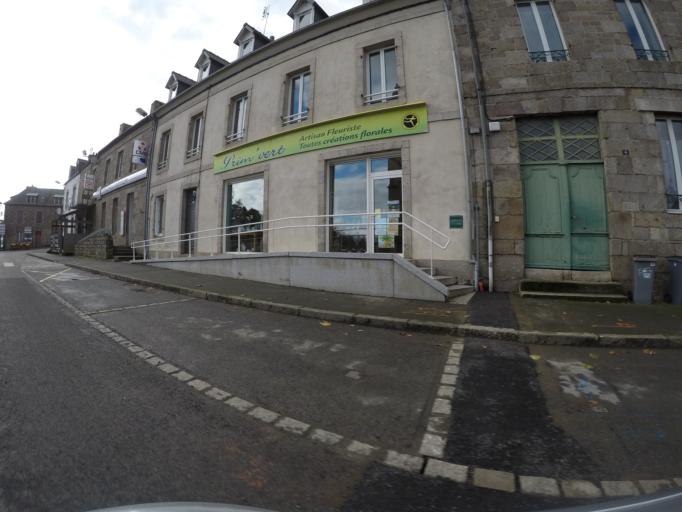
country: FR
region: Brittany
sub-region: Departement des Cotes-d'Armor
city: Bourbriac
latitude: 48.4735
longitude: -3.1879
